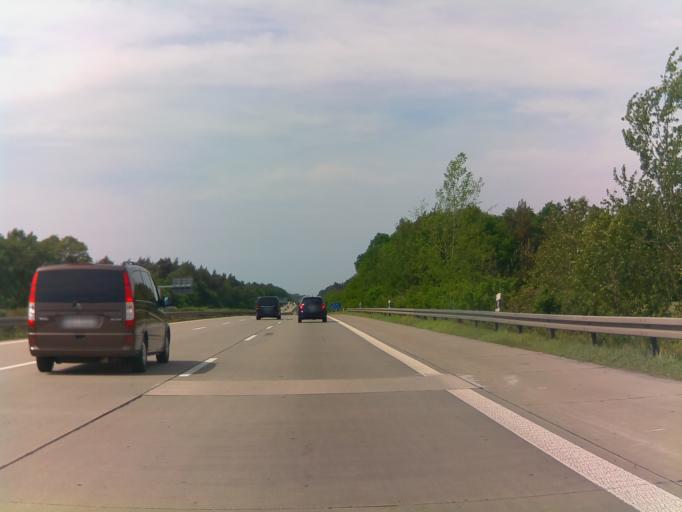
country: DE
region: Saxony-Anhalt
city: Burg bei Magdeburg
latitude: 52.2329
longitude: 11.8905
